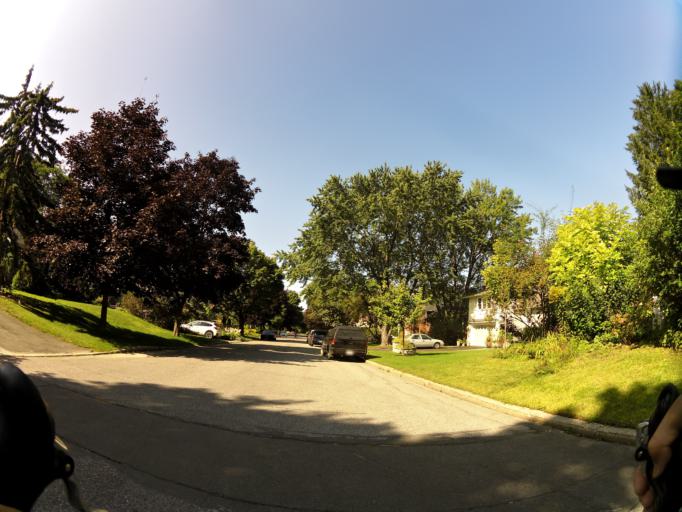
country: CA
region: Ontario
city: Ottawa
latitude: 45.3950
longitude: -75.6646
